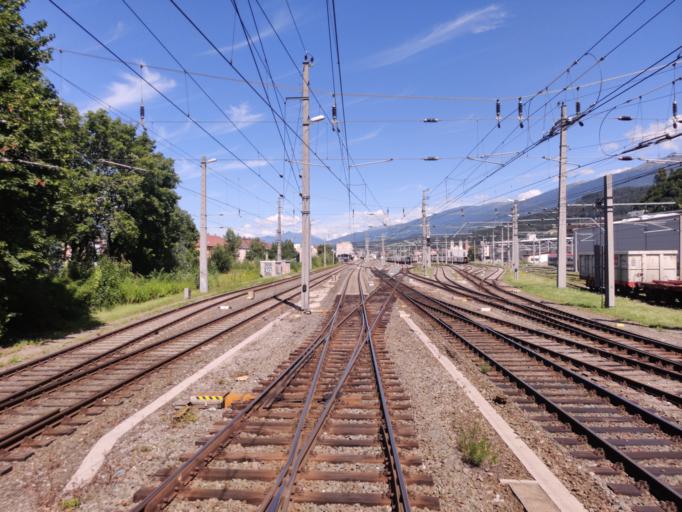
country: AT
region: Tyrol
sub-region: Innsbruck Stadt
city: Innsbruck
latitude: 47.2550
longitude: 11.3821
